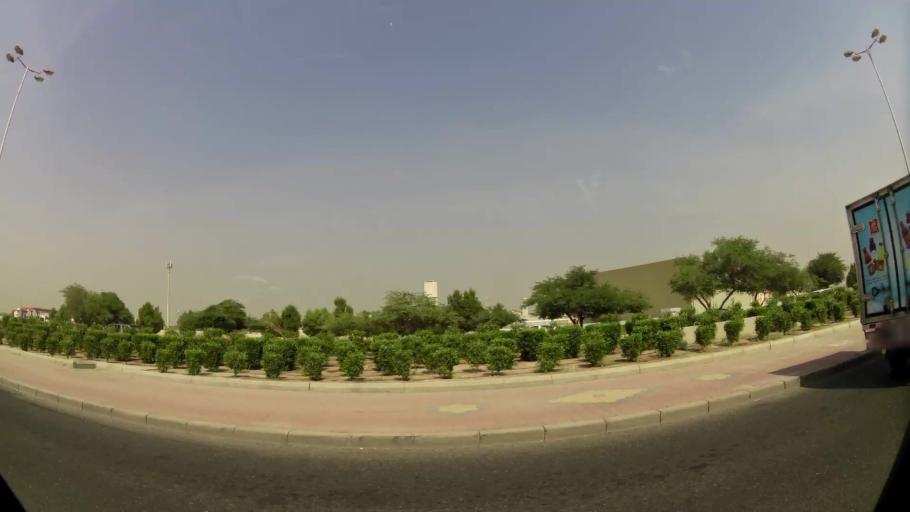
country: KW
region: Al Asimah
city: Ar Rabiyah
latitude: 29.3066
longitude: 47.8980
